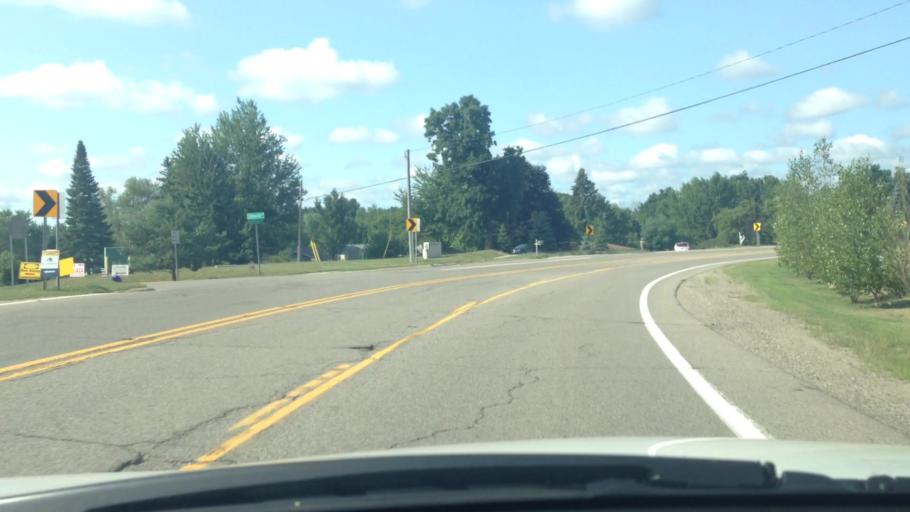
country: US
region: Michigan
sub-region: Oakland County
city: Clarkston
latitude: 42.7533
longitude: -83.3511
